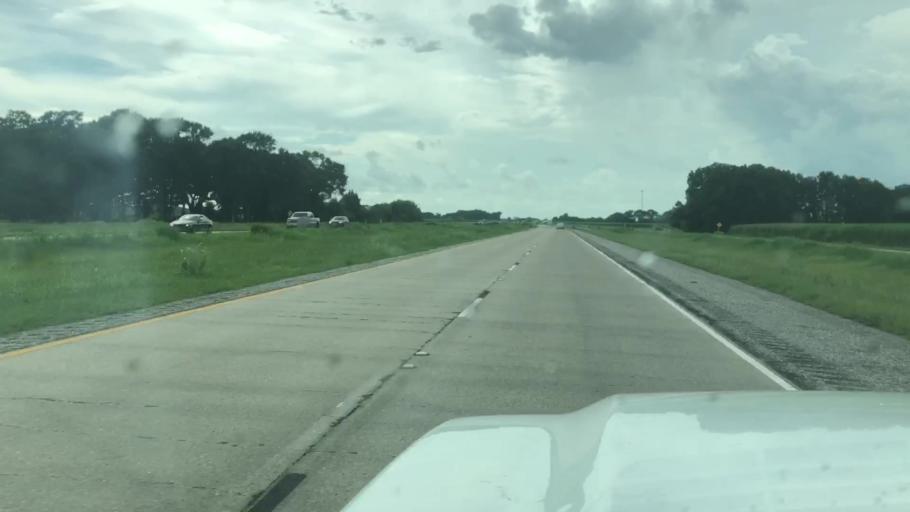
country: US
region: Louisiana
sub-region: Saint Mary Parish
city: Baldwin
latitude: 29.8563
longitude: -91.6097
